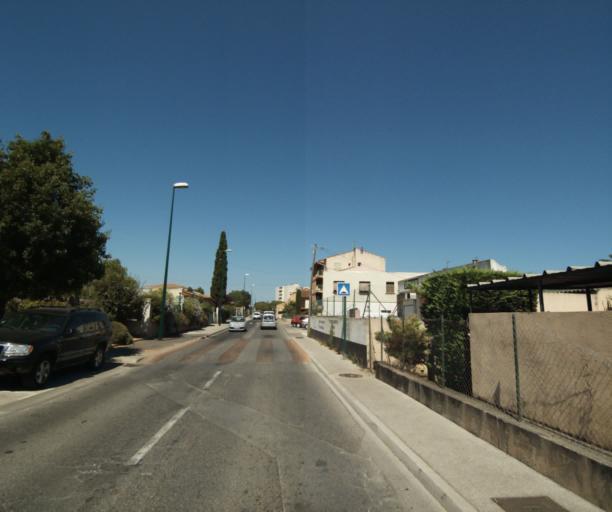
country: FR
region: Provence-Alpes-Cote d'Azur
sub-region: Departement du Var
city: La Garde
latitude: 43.1239
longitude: 6.0149
